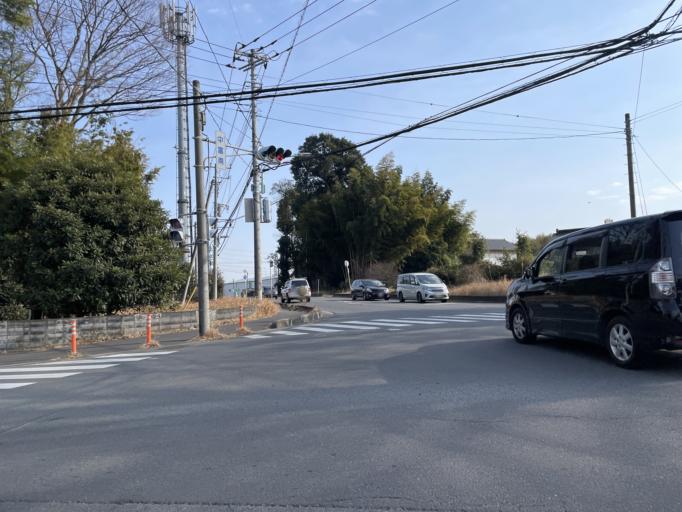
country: JP
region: Saitama
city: Tokorozawa
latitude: 35.8118
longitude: 139.4977
